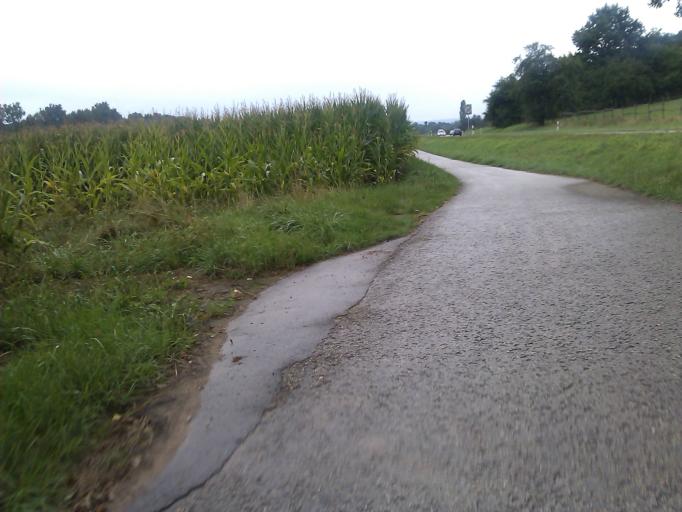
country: DE
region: Baden-Wuerttemberg
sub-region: Regierungsbezirk Stuttgart
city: Neckartenzlingen
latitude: 48.5740
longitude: 9.2275
